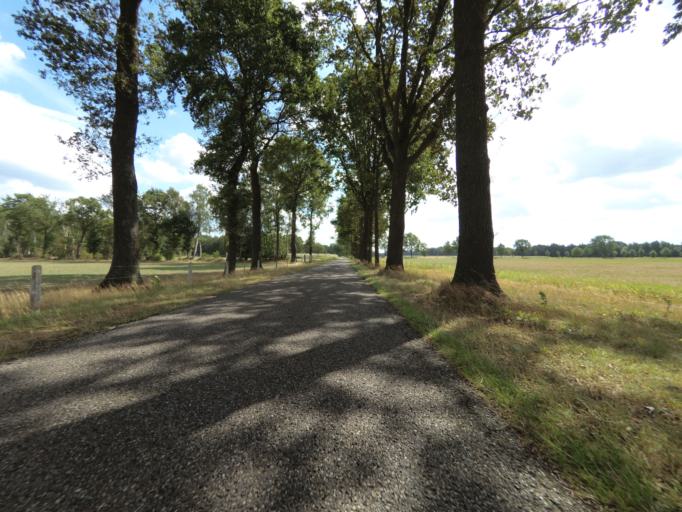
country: DE
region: North Rhine-Westphalia
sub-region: Regierungsbezirk Munster
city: Vreden
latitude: 52.1332
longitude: 6.8481
